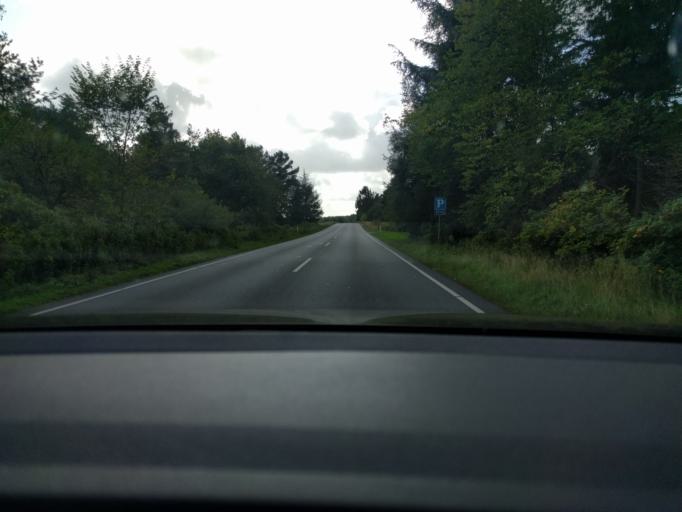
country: DK
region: Central Jutland
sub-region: Viborg Kommune
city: Bjerringbro
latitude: 56.2925
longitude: 9.6586
